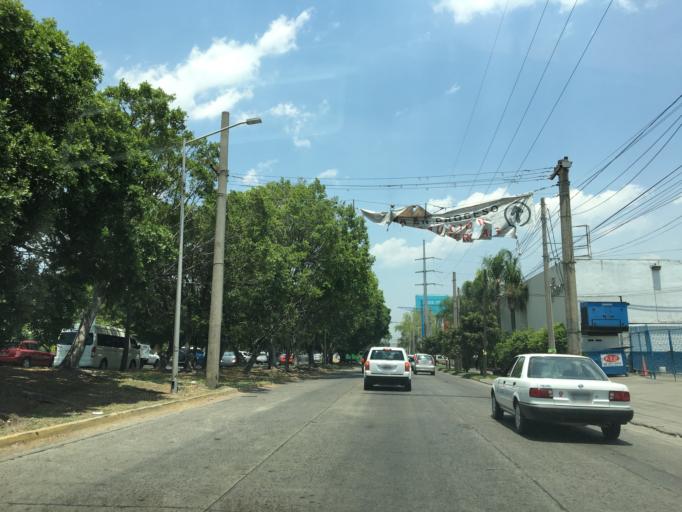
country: MX
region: Jalisco
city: Guadalajara
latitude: 20.6494
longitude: -103.3659
